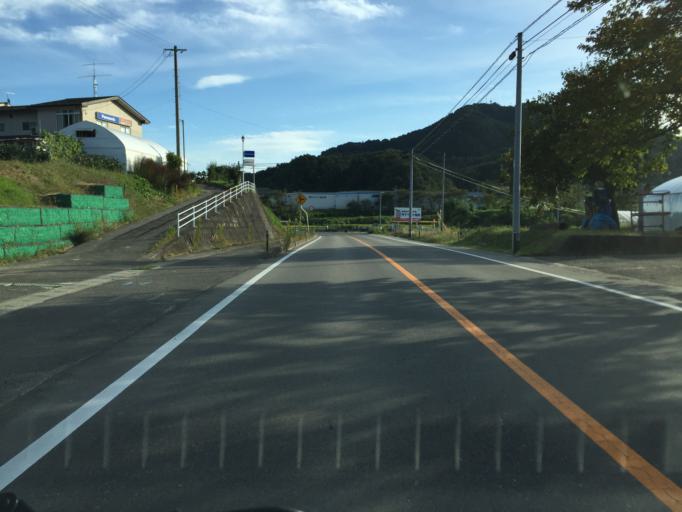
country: JP
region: Fukushima
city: Hobaramachi
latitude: 37.7675
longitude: 140.5955
